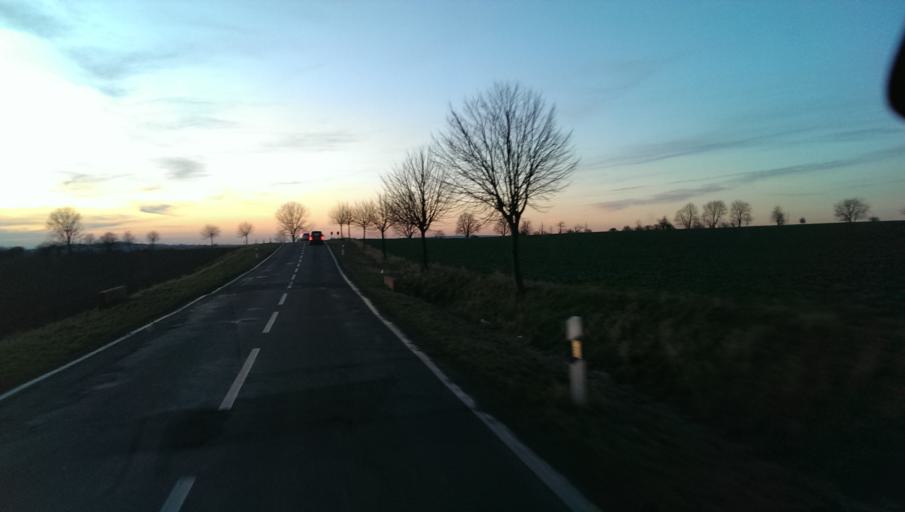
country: DE
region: Saxony-Anhalt
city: Ausleben
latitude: 52.0951
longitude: 11.1420
